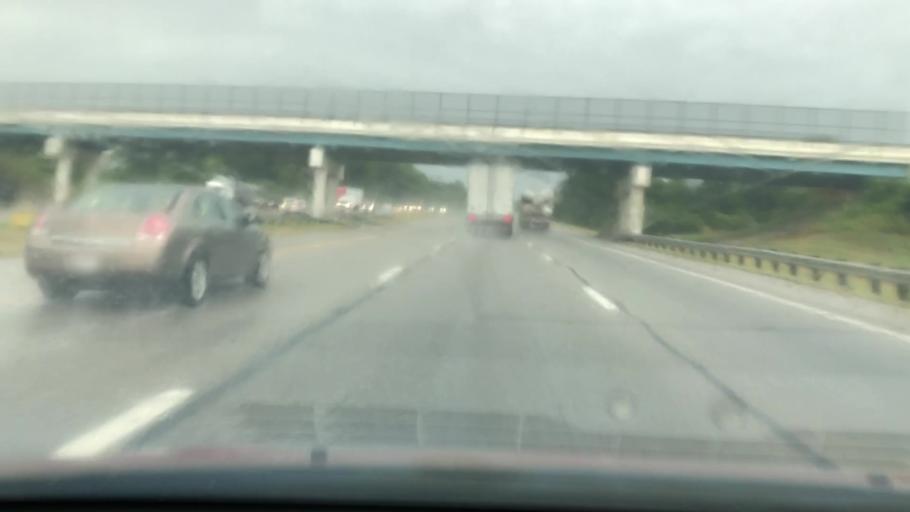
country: US
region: Ohio
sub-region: Madison County
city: Choctaw Lake
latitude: 39.9375
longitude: -83.5706
